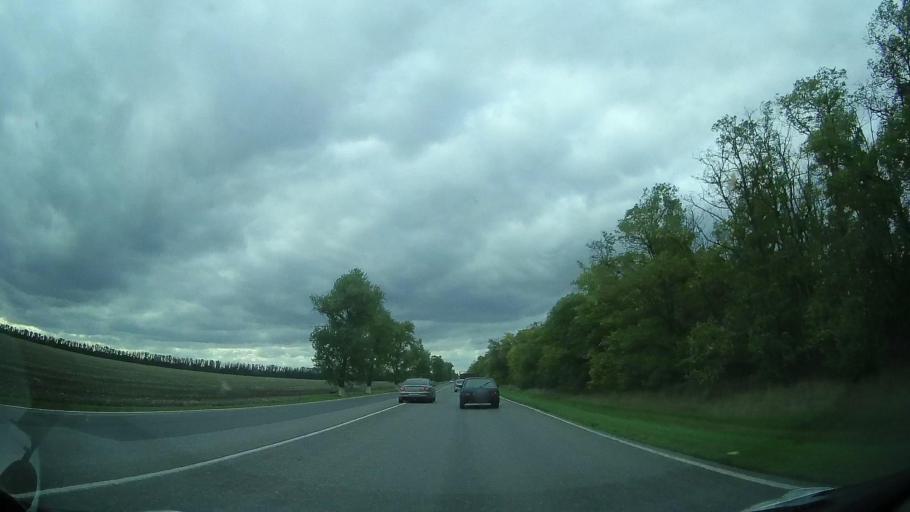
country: RU
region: Rostov
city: Zernograd
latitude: 46.8263
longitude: 40.2477
